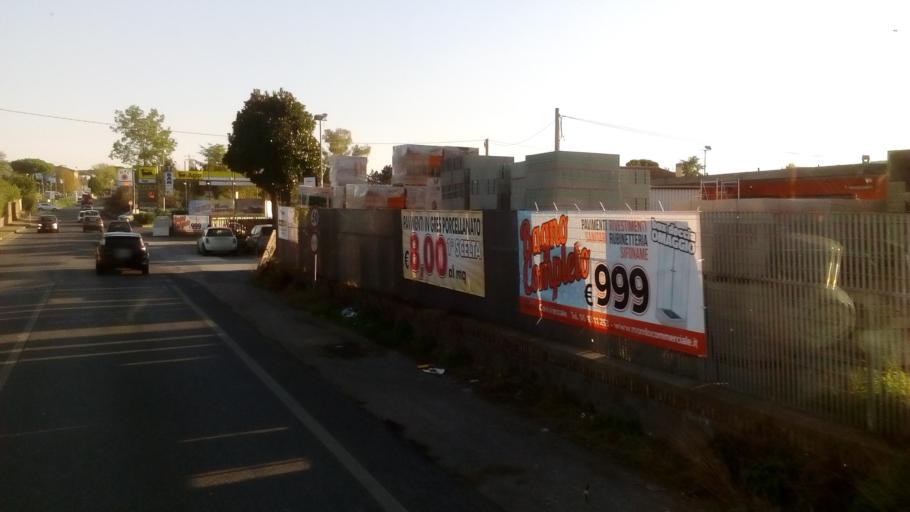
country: IT
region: Latium
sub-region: Citta metropolitana di Roma Capitale
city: Pavona
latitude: 41.7233
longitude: 12.6192
